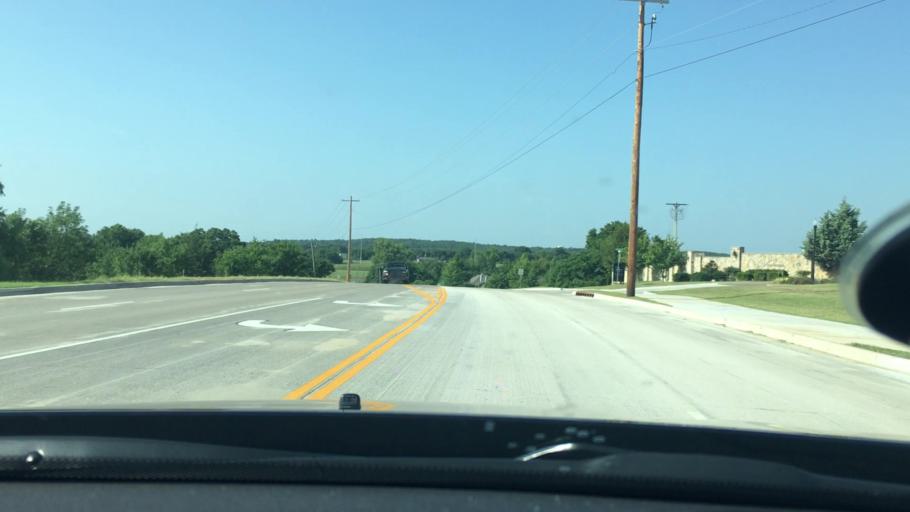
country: US
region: Oklahoma
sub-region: Pontotoc County
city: Ada
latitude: 34.7573
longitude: -96.6697
